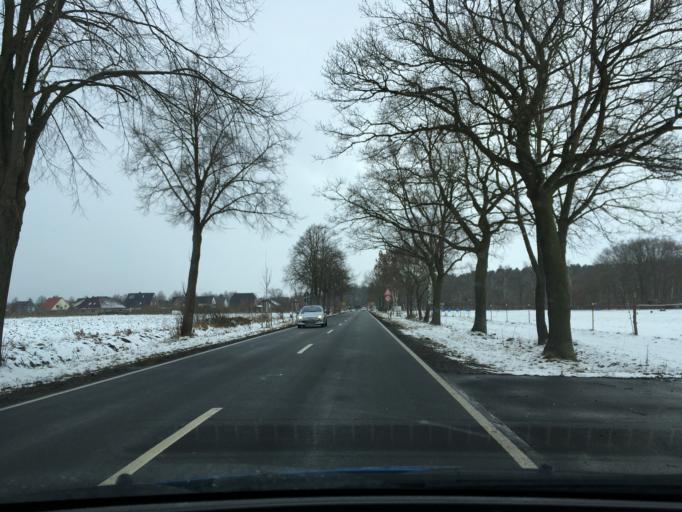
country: DE
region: Lower Saxony
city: Garstedt
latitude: 53.2984
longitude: 10.1886
